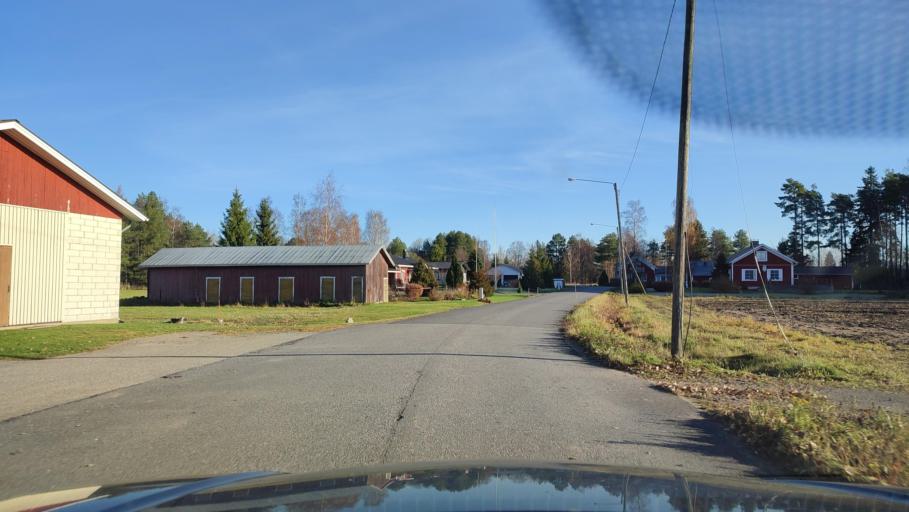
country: FI
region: Southern Ostrobothnia
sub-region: Suupohja
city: Karijoki
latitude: 62.2295
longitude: 21.6515
